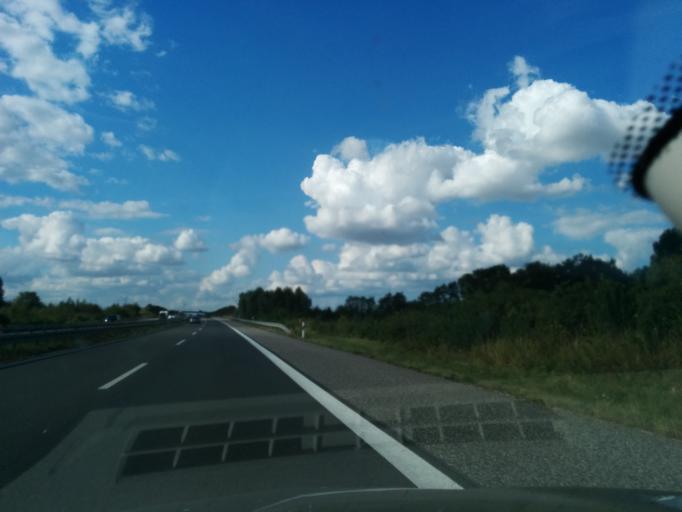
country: DE
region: Brandenburg
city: Grunow
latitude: 53.3368
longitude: 13.9833
